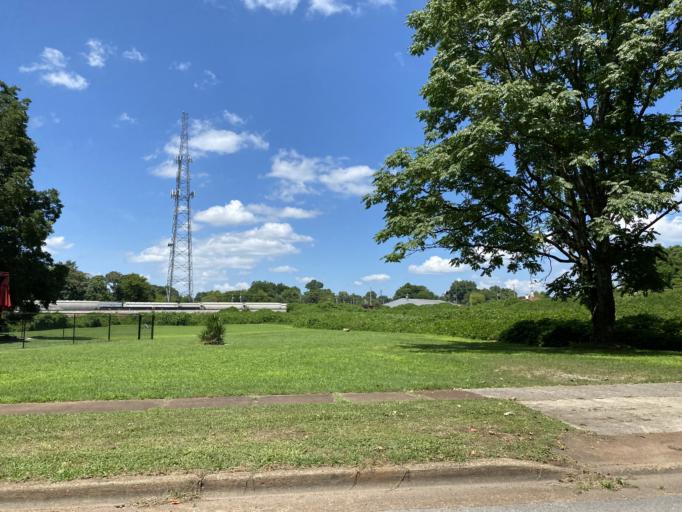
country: US
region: Alabama
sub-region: Morgan County
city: Decatur
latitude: 34.6119
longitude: -86.9893
